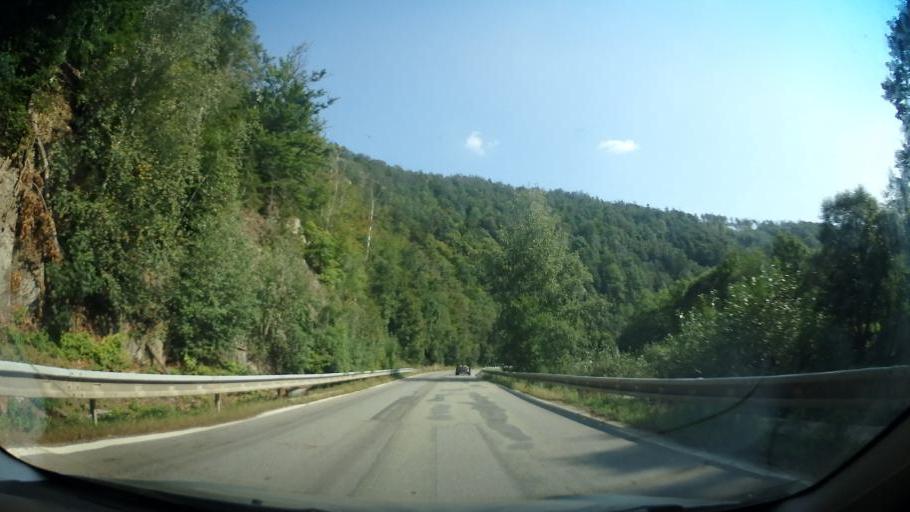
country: CZ
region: Pardubicky
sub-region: Okres Svitavy
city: Bystre
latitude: 49.5496
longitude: 16.3413
